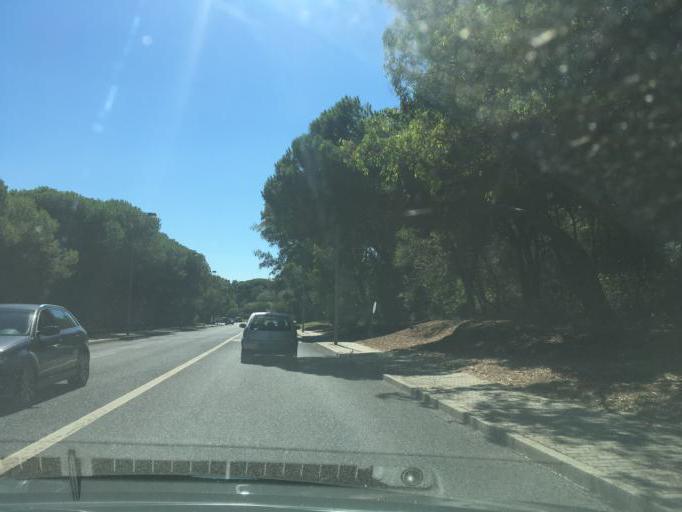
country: PT
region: Lisbon
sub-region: Oeiras
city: Alges
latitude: 38.7171
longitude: -9.2000
